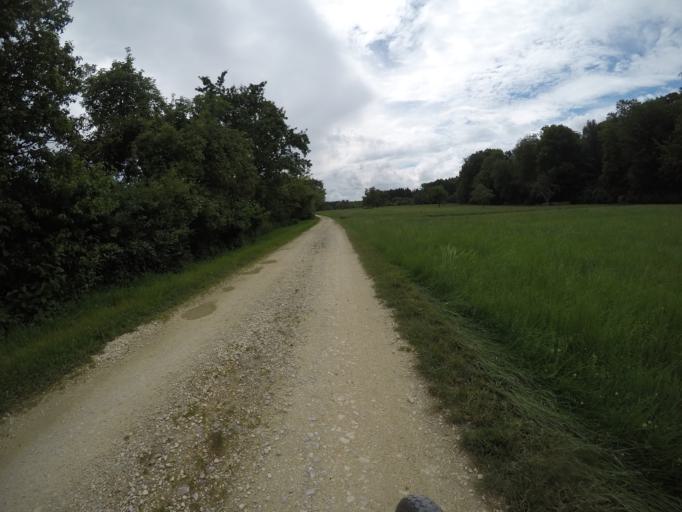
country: DE
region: Baden-Wuerttemberg
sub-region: Tuebingen Region
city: Dornstadt
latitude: 48.4770
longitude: 9.9565
